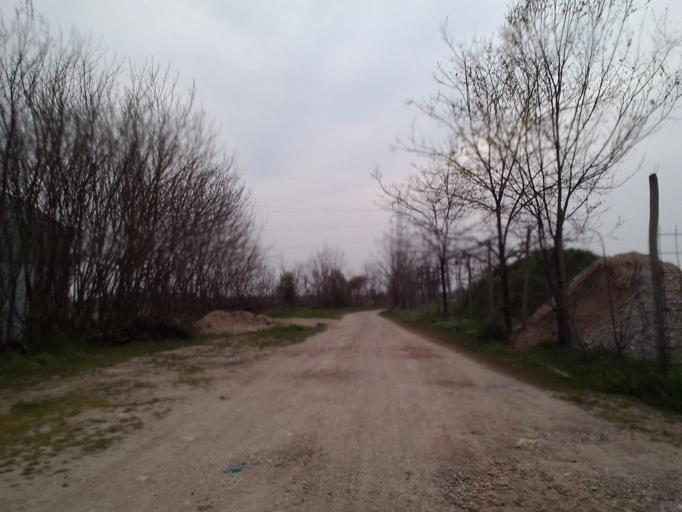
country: IT
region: Veneto
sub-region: Provincia di Verona
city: Povegliano Veronese
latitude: 45.3697
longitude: 10.8921
